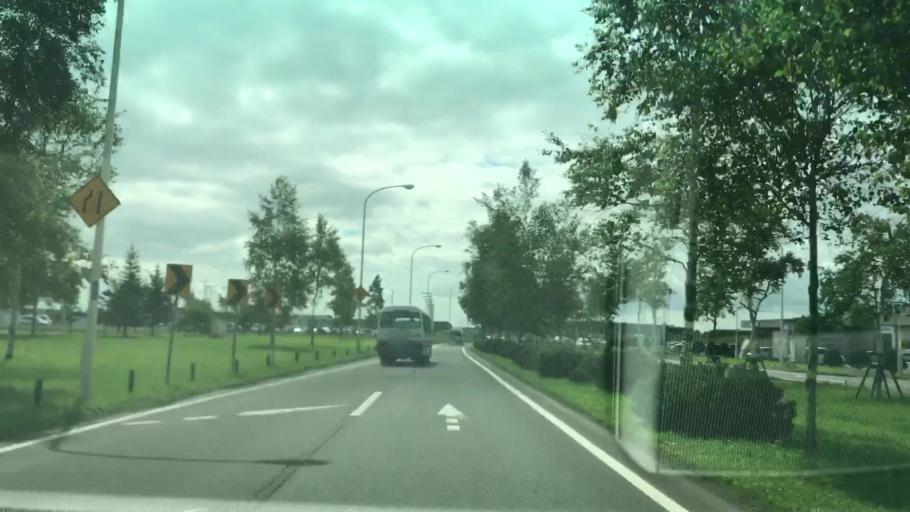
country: JP
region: Hokkaido
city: Chitose
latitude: 42.7829
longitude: 141.6776
